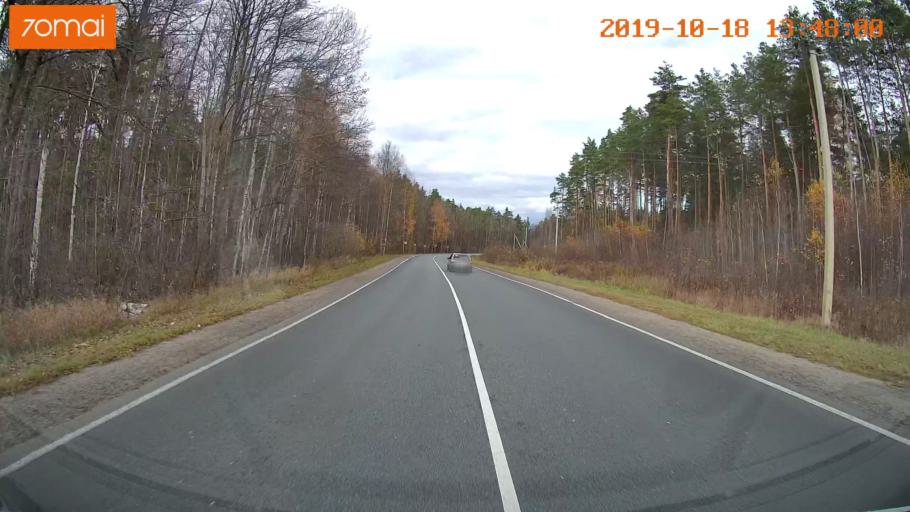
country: RU
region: Moskovskaya
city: Radovitskiy
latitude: 54.9834
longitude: 39.9518
